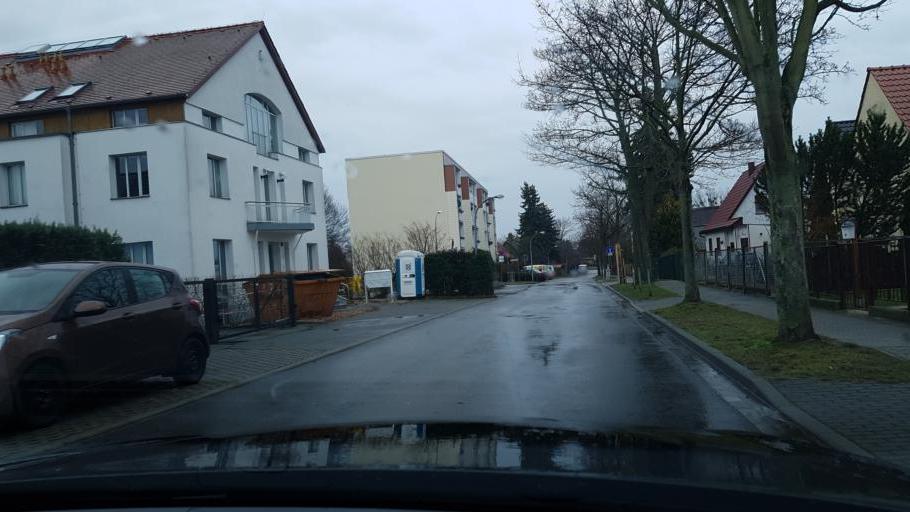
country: DE
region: Berlin
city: Altglienicke
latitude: 52.3963
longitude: 13.5313
